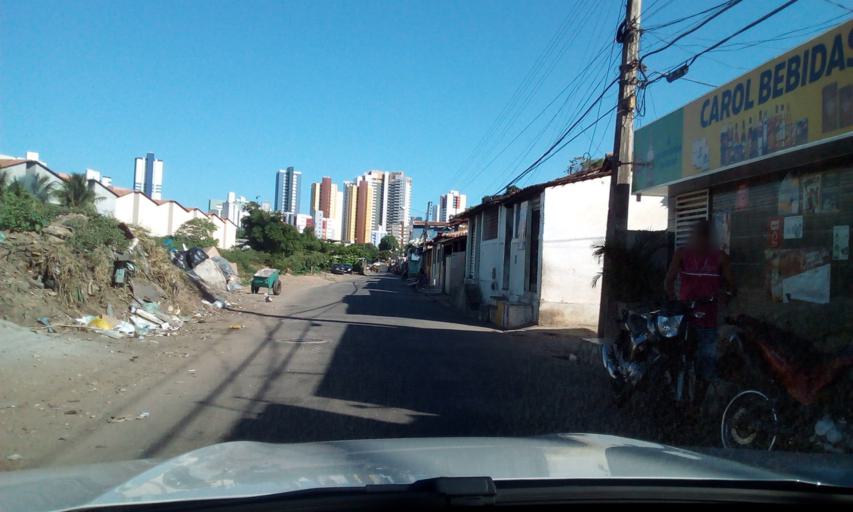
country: BR
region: Paraiba
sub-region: Joao Pessoa
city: Joao Pessoa
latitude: -7.1119
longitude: -34.8355
